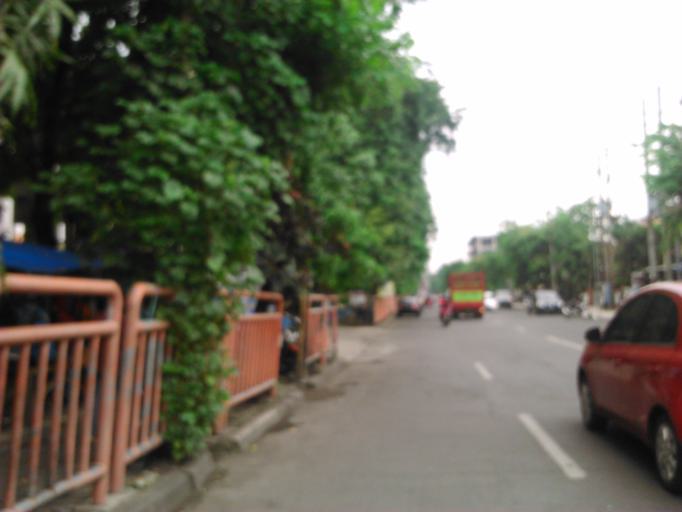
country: ID
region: East Java
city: Gubengairlangga
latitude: -7.2707
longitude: 112.7602
